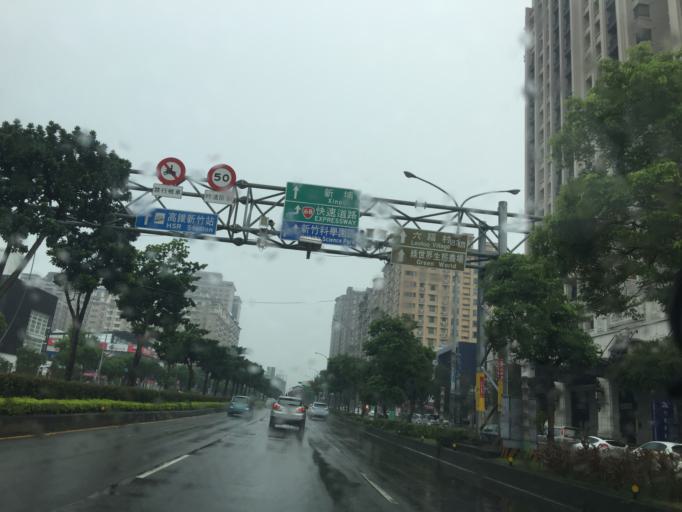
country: TW
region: Taiwan
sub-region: Hsinchu
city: Zhubei
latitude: 24.8215
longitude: 121.0230
